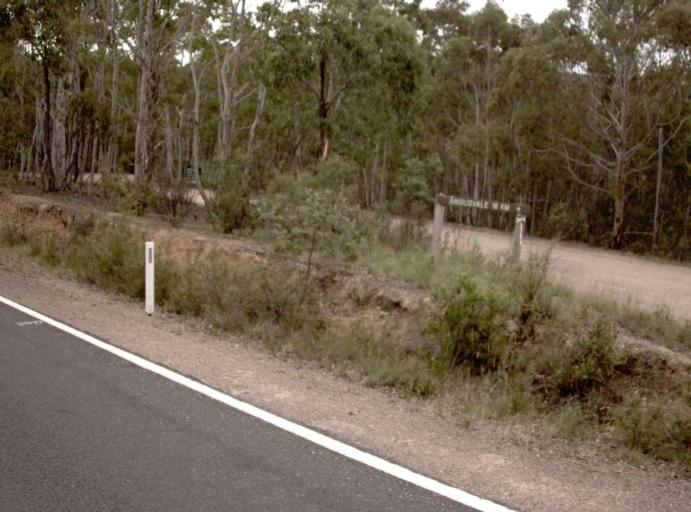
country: AU
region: Victoria
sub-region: East Gippsland
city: Bairnsdale
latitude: -37.6448
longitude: 147.2763
